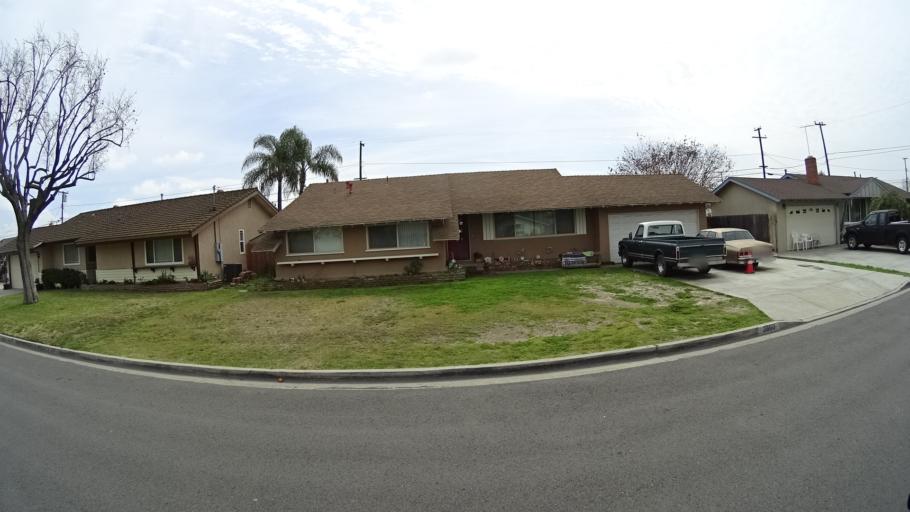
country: US
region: California
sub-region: Orange County
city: Stanton
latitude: 33.8186
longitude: -117.9876
